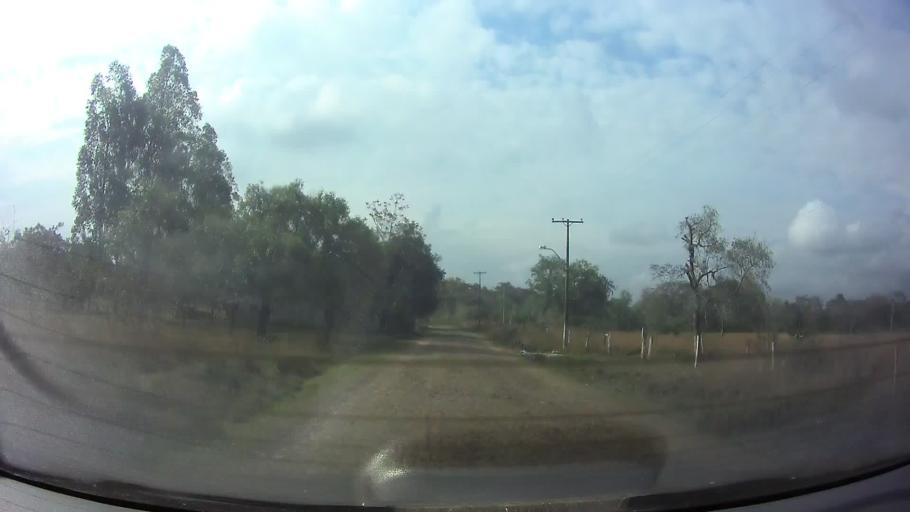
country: PY
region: Cordillera
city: Arroyos y Esteros
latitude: -24.9992
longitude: -57.1949
